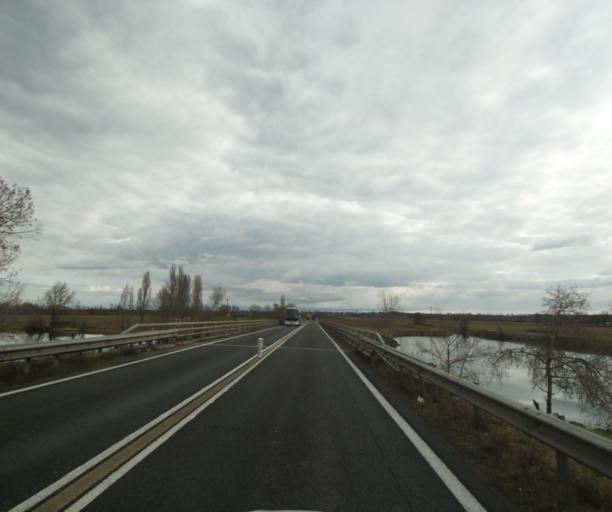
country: FR
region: Auvergne
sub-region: Departement de l'Allier
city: Toulon-sur-Allier
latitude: 46.4833
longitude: 3.3358
